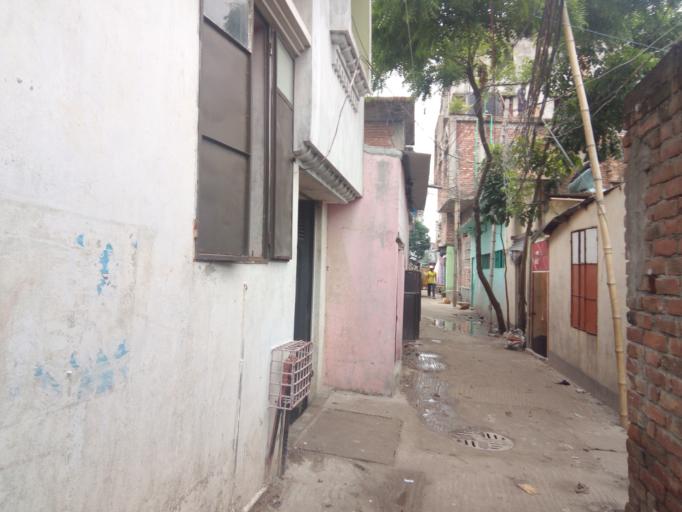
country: BD
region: Dhaka
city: Azimpur
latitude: 23.7171
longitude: 90.3730
